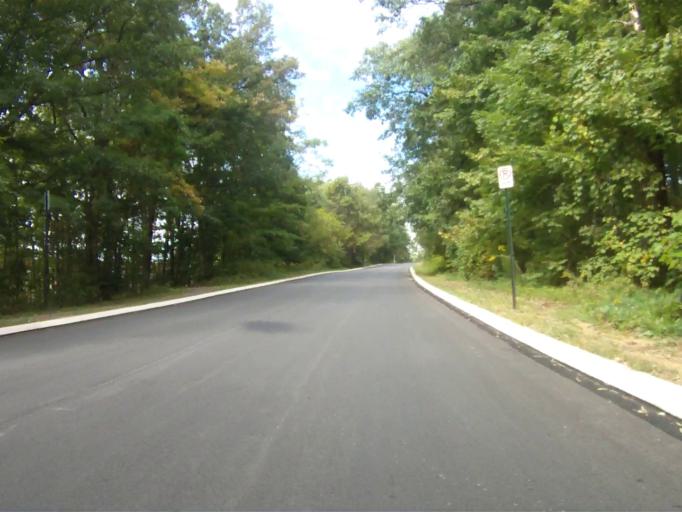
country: US
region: Pennsylvania
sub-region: Centre County
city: Park Forest Village
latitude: 40.8054
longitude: -77.9207
